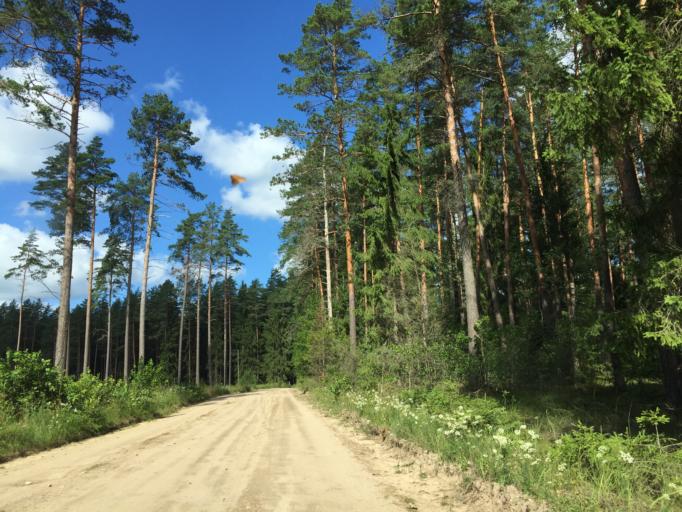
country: LV
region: Garkalne
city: Garkalne
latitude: 56.9719
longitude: 24.4653
